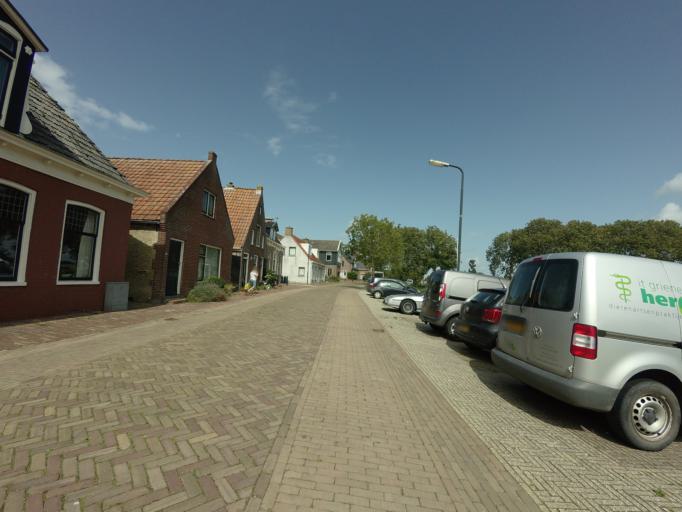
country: NL
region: Friesland
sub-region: Gemeente Harlingen
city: Harlingen
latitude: 53.1146
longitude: 5.4415
